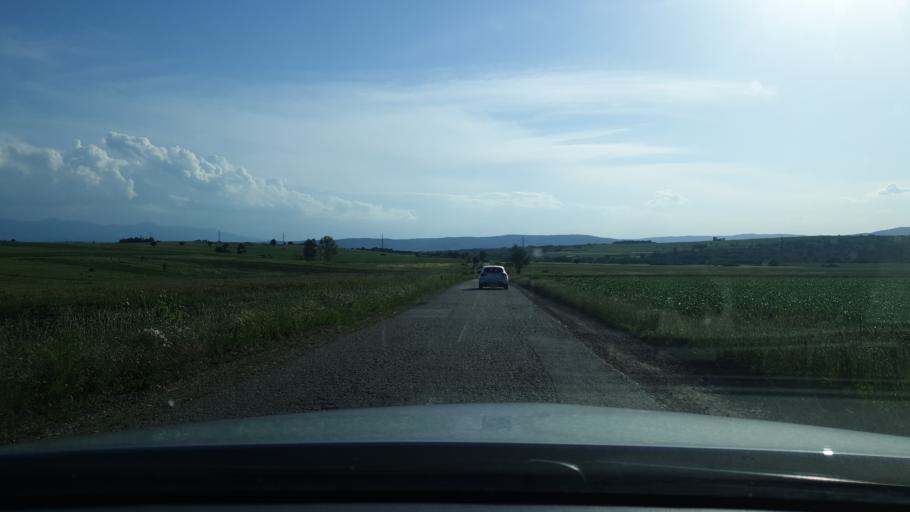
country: RS
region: Central Serbia
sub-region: Nisavski Okrug
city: Aleksinac
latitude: 43.6145
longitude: 21.6652
